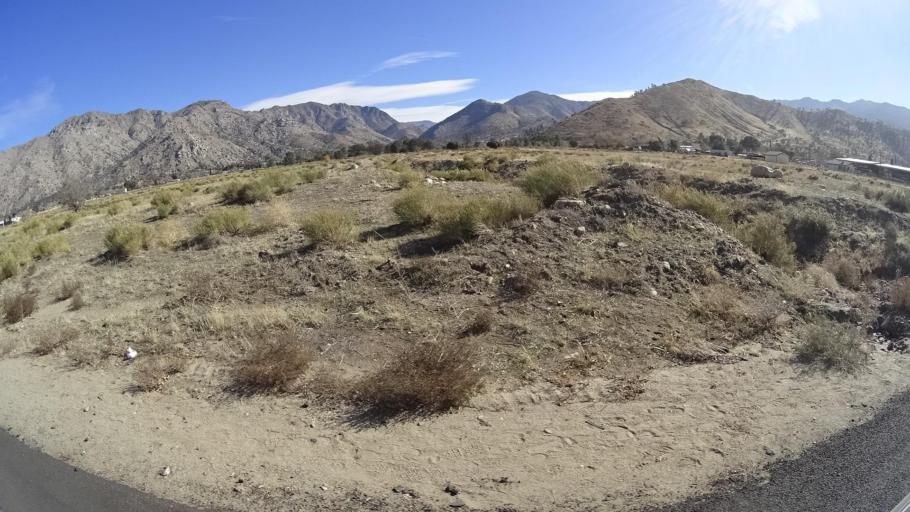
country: US
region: California
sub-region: Kern County
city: Lake Isabella
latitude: 35.6082
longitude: -118.4844
